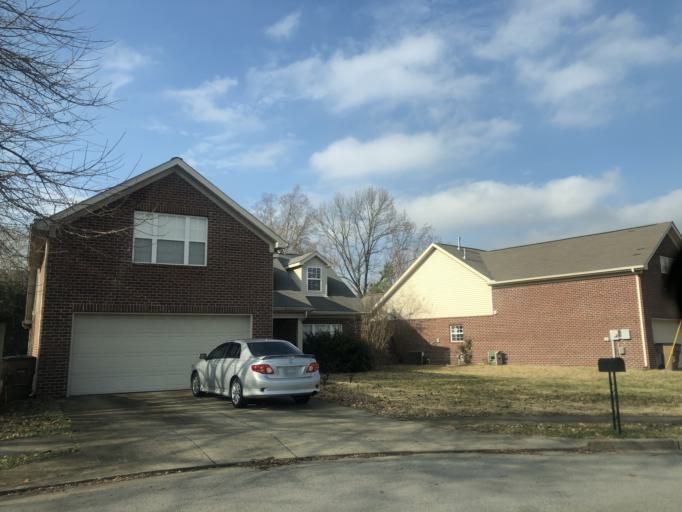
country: US
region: Tennessee
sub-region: Davidson County
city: Oak Hill
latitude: 36.1034
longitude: -86.7200
